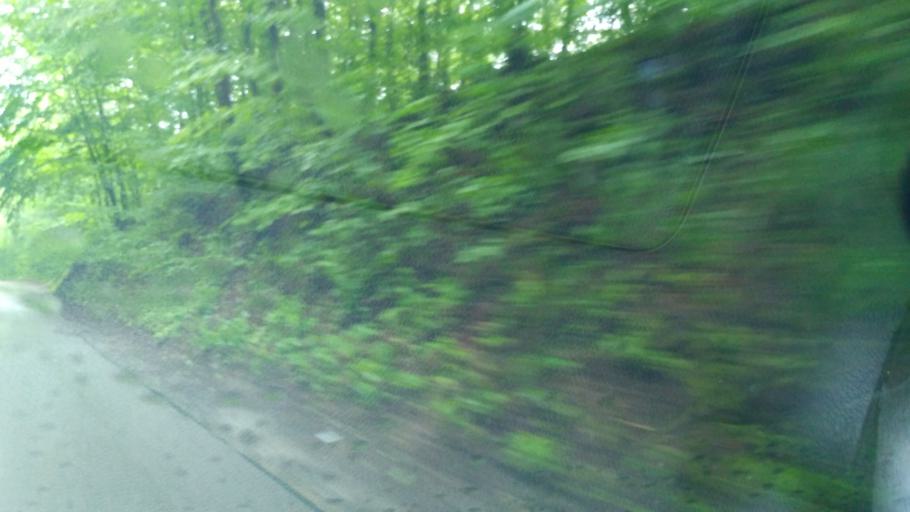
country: PL
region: Subcarpathian Voivodeship
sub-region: Powiat jasielski
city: Jaslo
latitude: 49.7927
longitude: 21.4924
